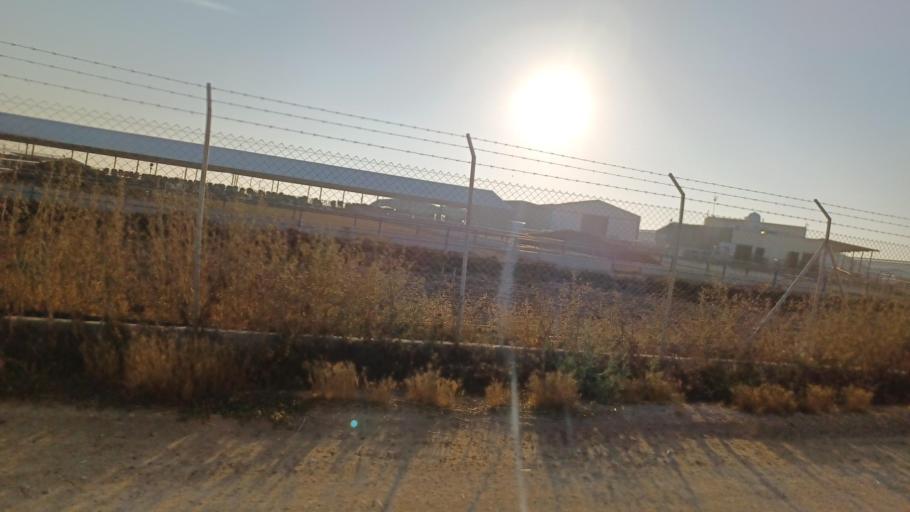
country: CY
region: Ammochostos
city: Achna
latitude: 35.0189
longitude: 33.7983
